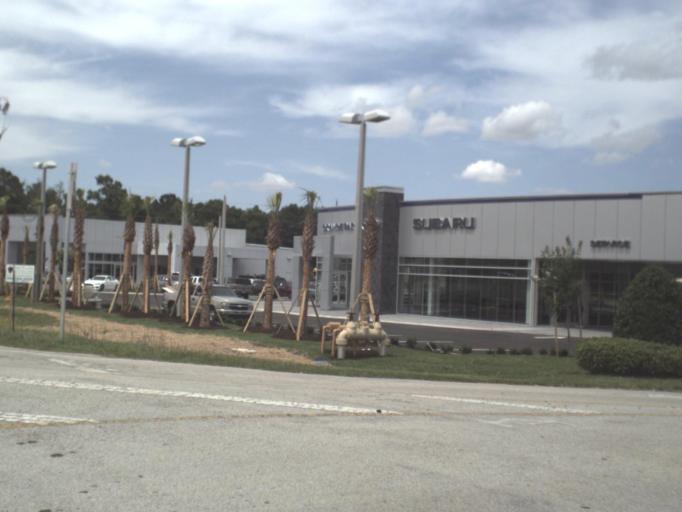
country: US
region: Florida
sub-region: Clay County
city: Bellair-Meadowbrook Terrace
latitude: 30.2208
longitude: -81.7368
